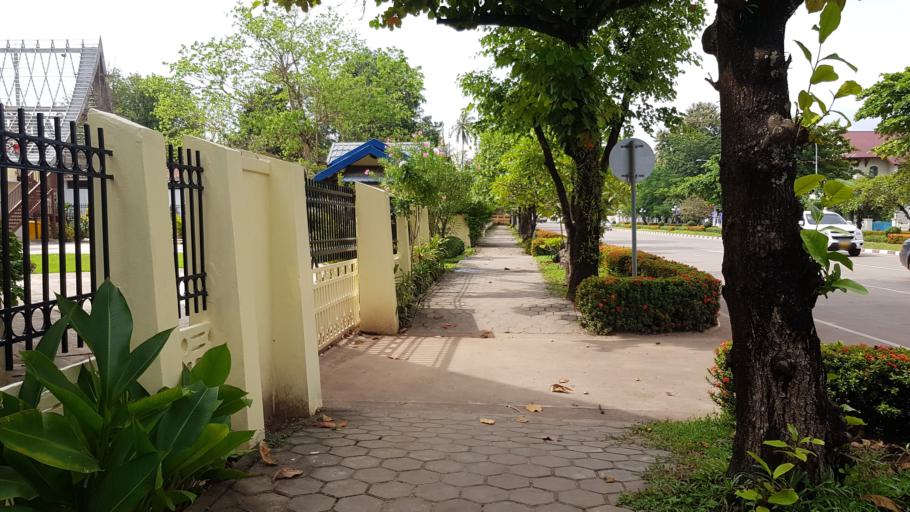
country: LA
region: Vientiane
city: Vientiane
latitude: 17.9641
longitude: 102.6120
